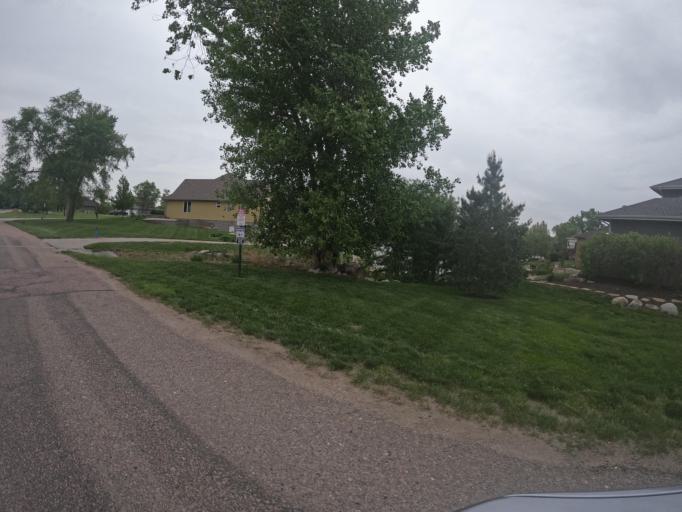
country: US
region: Nebraska
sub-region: Sarpy County
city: Offutt Air Force Base
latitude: 41.0502
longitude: -95.9579
